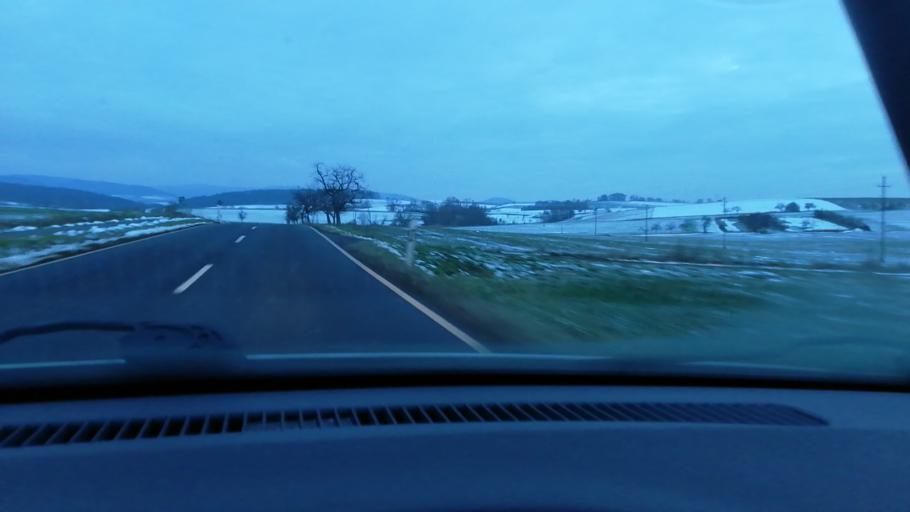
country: DE
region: Bavaria
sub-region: Regierungsbezirk Unterfranken
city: Geiselbach
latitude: 50.1177
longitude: 9.2032
